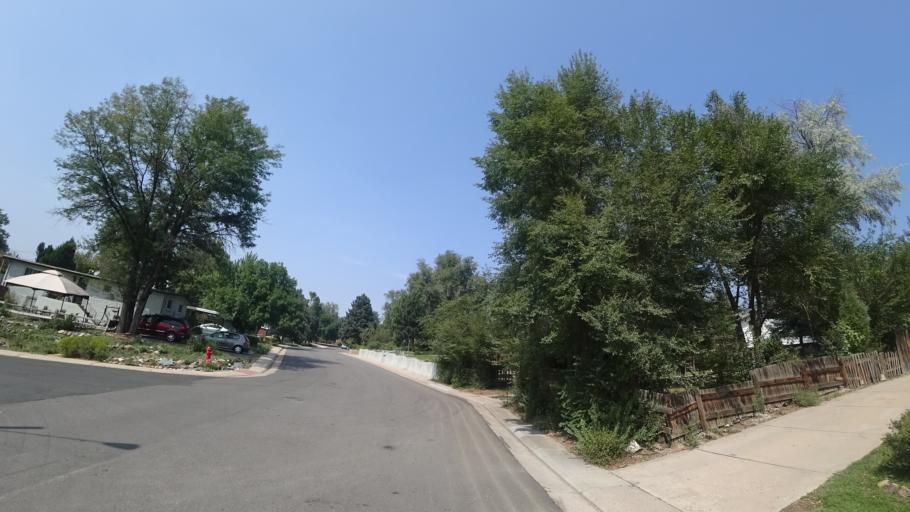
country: US
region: Colorado
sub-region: Arapahoe County
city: Littleton
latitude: 39.6262
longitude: -104.9988
